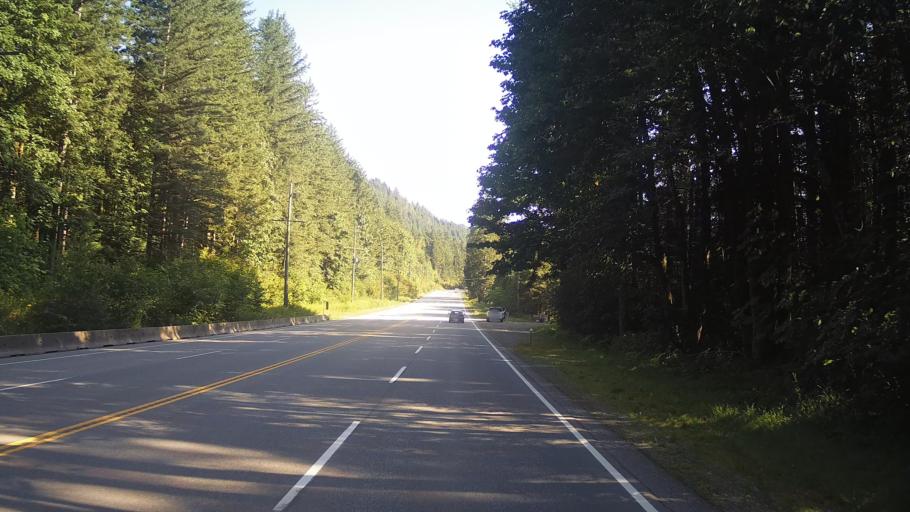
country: CA
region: British Columbia
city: Hope
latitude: 49.4563
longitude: -121.4361
